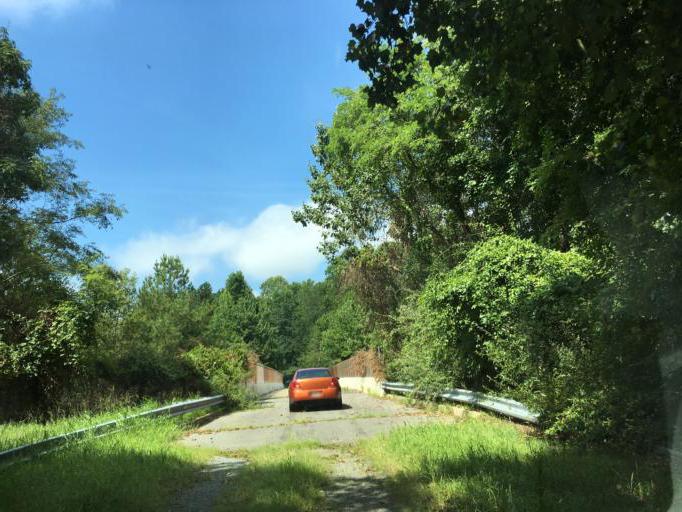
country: US
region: Maryland
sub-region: Anne Arundel County
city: Crownsville
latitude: 39.0187
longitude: -76.6132
